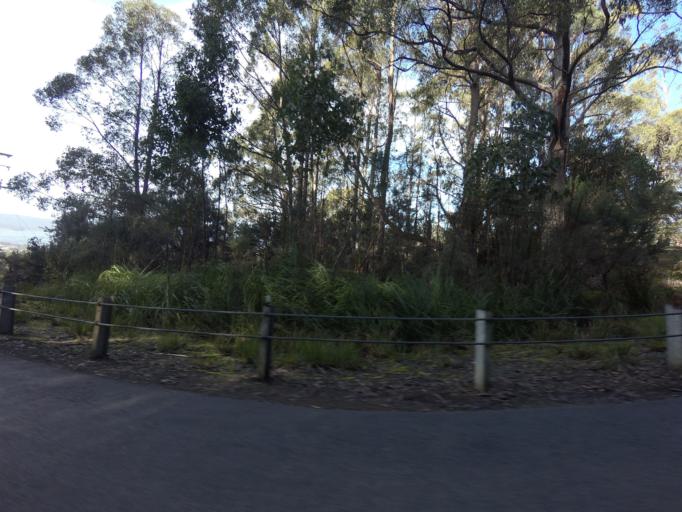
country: AU
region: Tasmania
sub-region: Kingborough
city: Kettering
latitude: -43.1699
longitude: 147.2037
